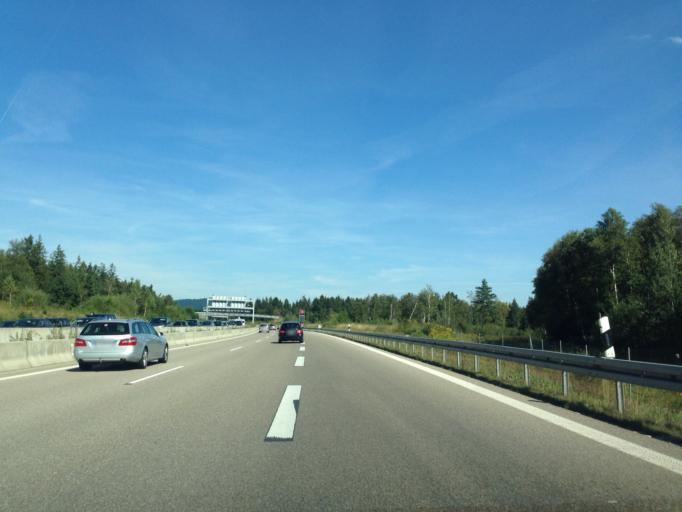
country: AT
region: Tyrol
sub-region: Politischer Bezirk Reutte
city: Vils
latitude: 47.5768
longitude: 10.6621
